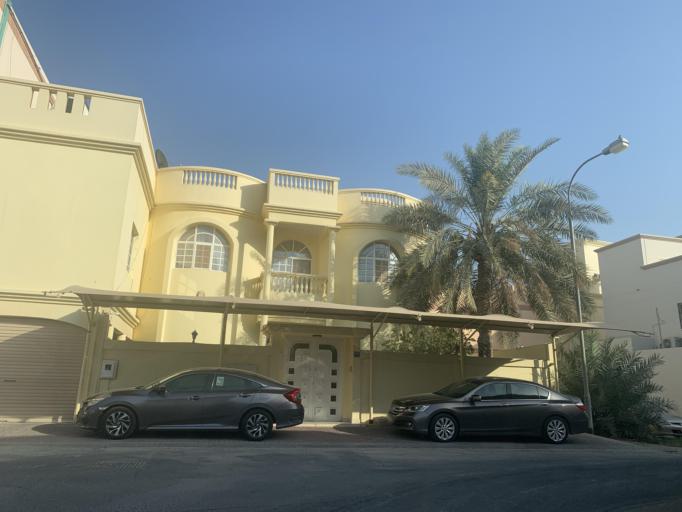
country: BH
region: Manama
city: Jidd Hafs
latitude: 26.2094
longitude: 50.5324
